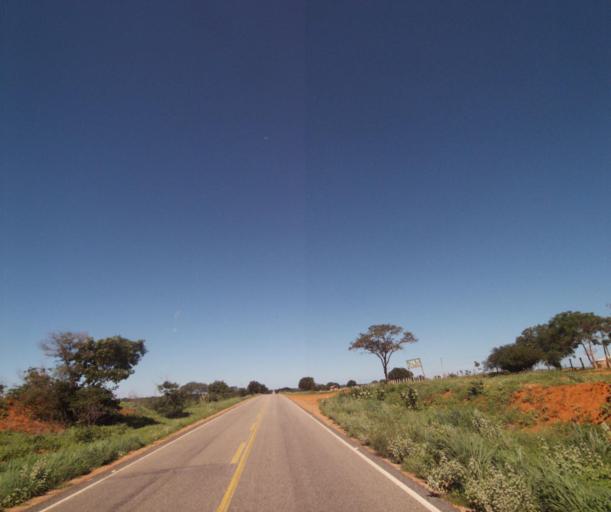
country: BR
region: Bahia
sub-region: Palmas De Monte Alto
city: Palmas de Monte Alto
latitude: -14.2592
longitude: -43.2825
